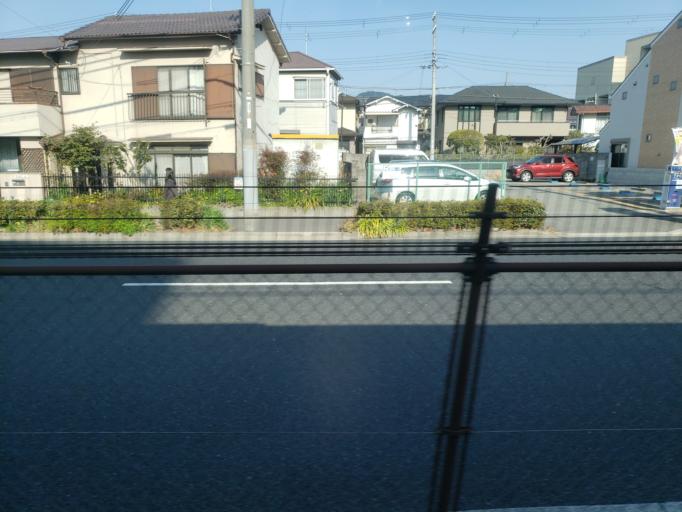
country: JP
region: Hyogo
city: Kobe
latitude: 34.6449
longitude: 135.1224
